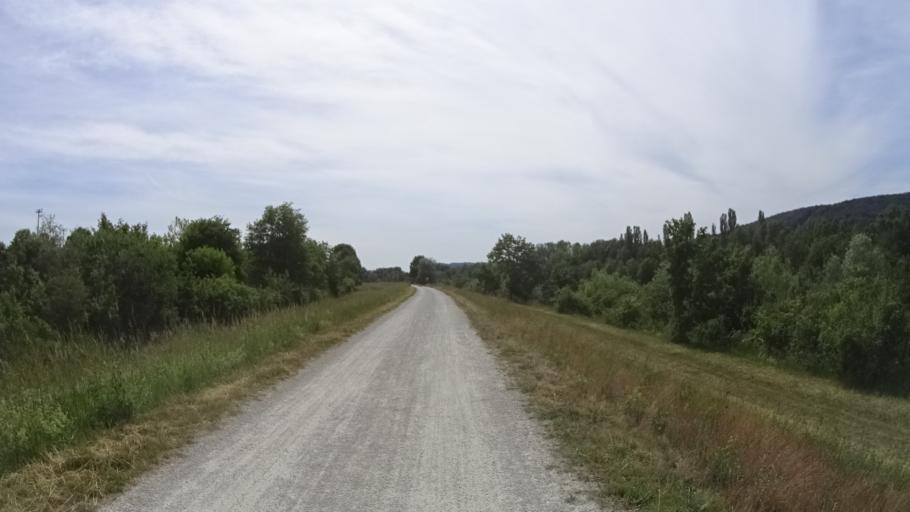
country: DE
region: Bavaria
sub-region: Lower Bavaria
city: Kelheim
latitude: 48.9131
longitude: 11.8842
